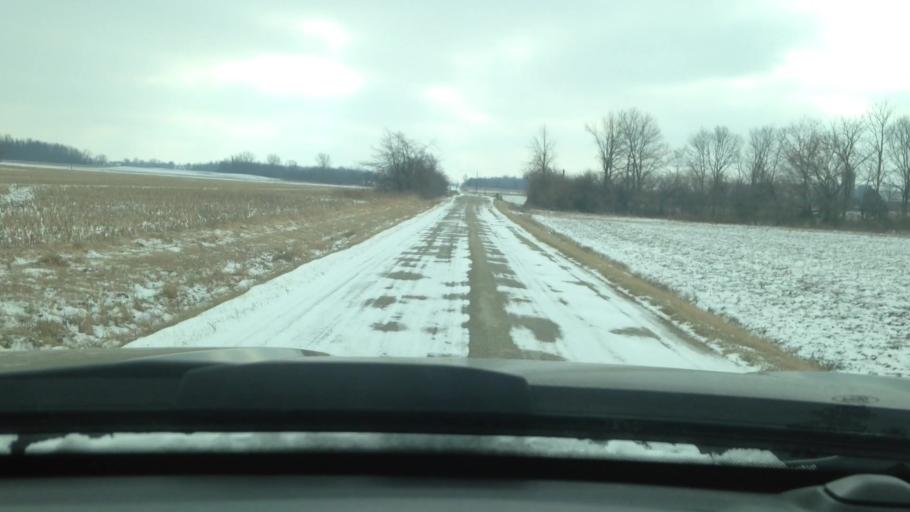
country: US
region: Indiana
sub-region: Randolph County
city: Union City
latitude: 40.2695
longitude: -84.8622
